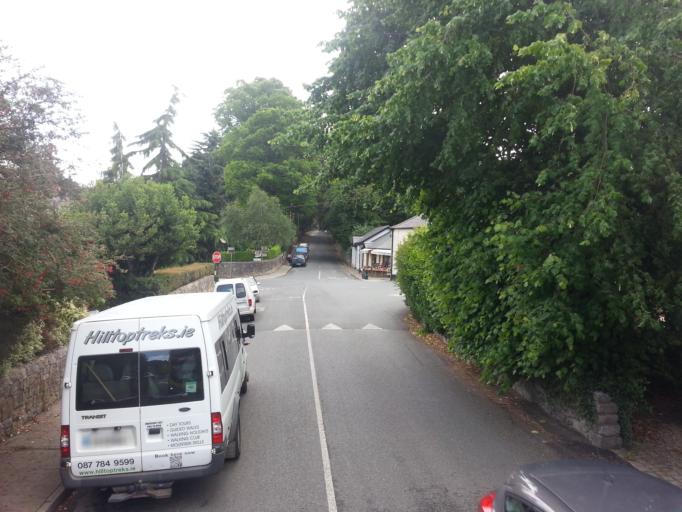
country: IE
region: Leinster
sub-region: Wicklow
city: Enniskerry
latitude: 53.1934
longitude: -6.1733
